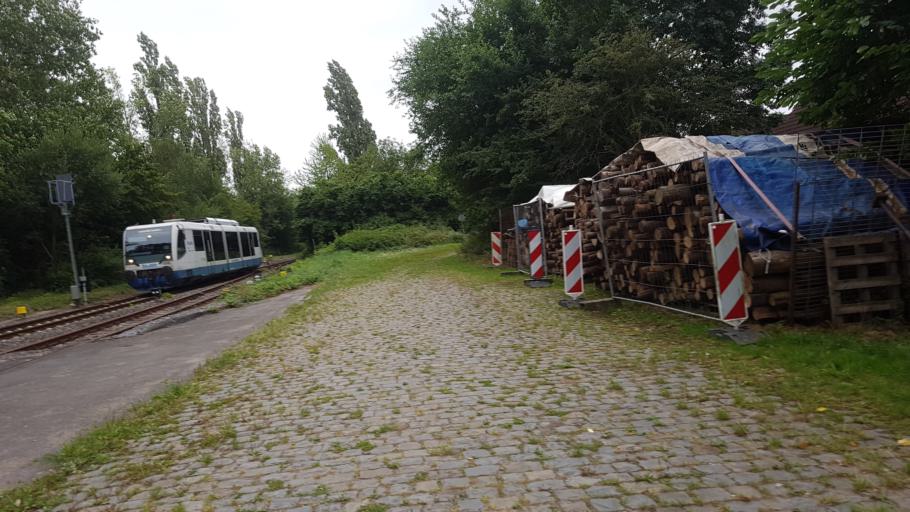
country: DE
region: North Rhine-Westphalia
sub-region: Regierungsbezirk Koln
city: Niederzier
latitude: 50.8769
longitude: 6.4253
